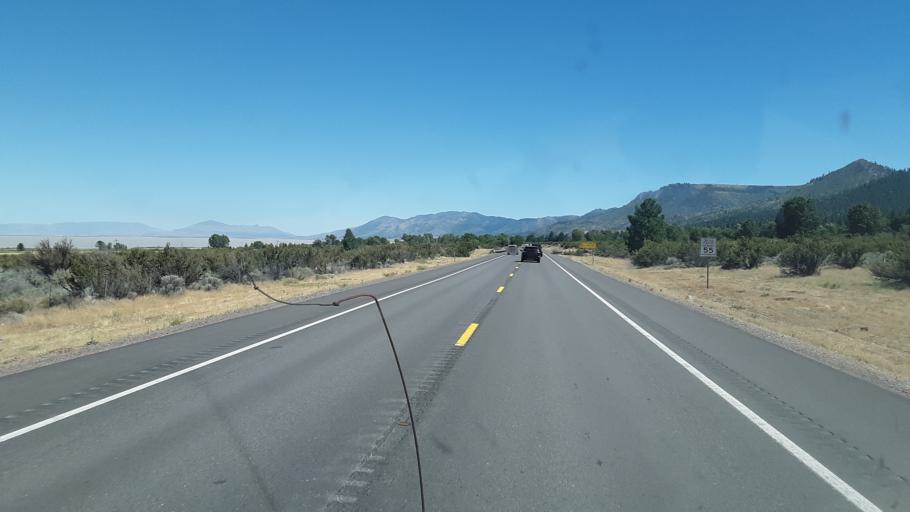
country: US
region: California
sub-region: Lassen County
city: Janesville
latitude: 40.2801
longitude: -120.4872
